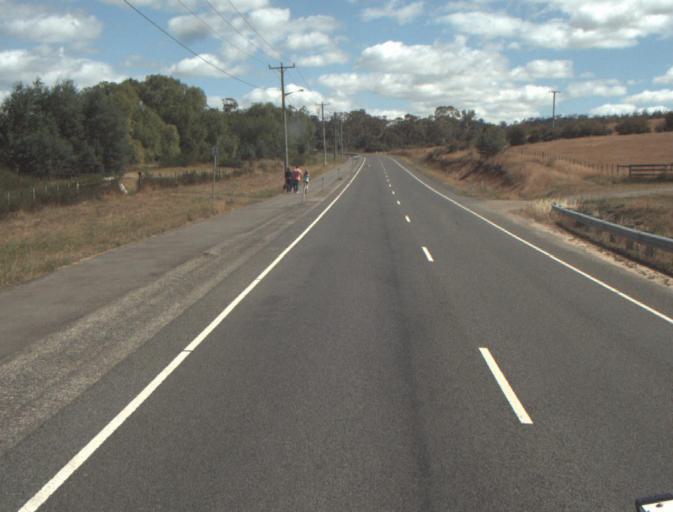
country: AU
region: Tasmania
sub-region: Launceston
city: Newstead
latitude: -41.4288
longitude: 147.1868
